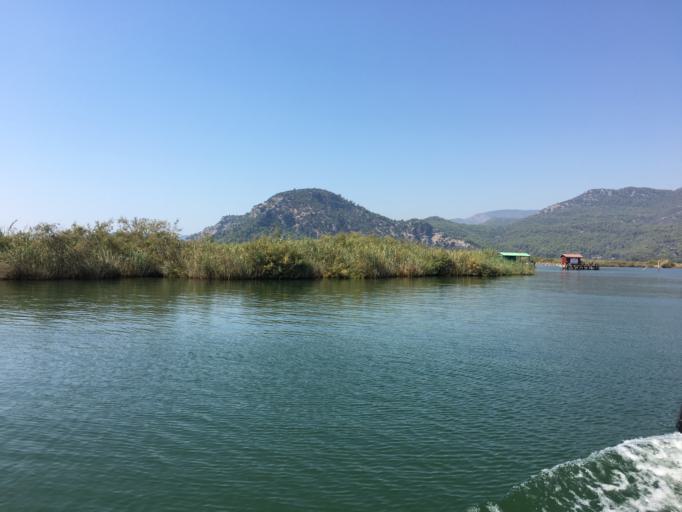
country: TR
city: Dalyan
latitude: 36.8154
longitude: 28.6282
